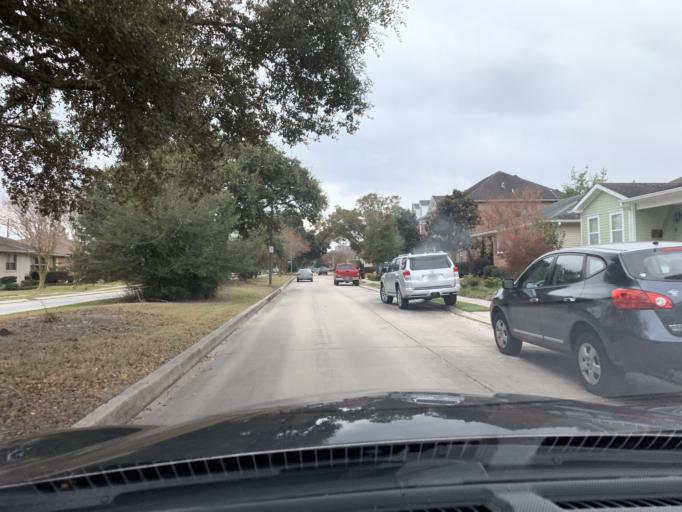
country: US
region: Louisiana
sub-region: Jefferson Parish
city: Metairie
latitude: 30.0072
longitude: -90.1024
